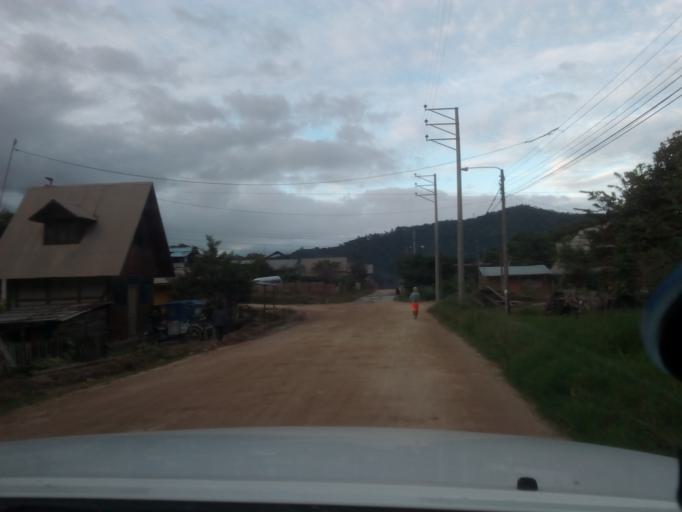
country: PE
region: Pasco
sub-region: Provincia de Oxapampa
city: Villa Rica
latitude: -10.7406
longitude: -75.2740
